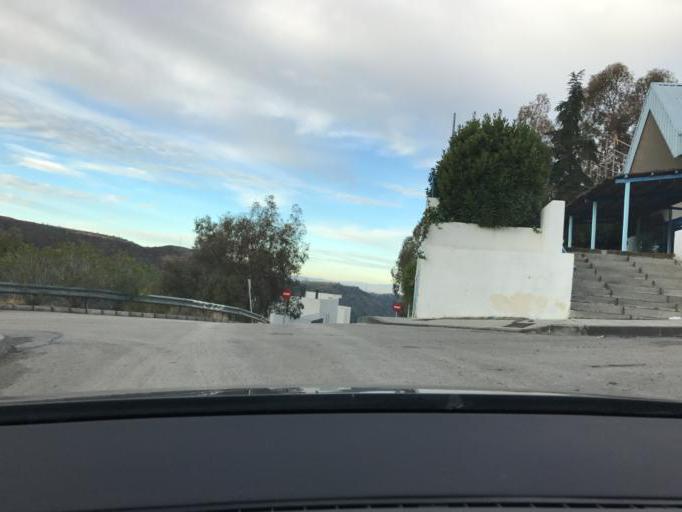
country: ES
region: Andalusia
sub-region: Provincia de Granada
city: Cenes de la Vega
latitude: 37.1654
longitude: -3.5443
